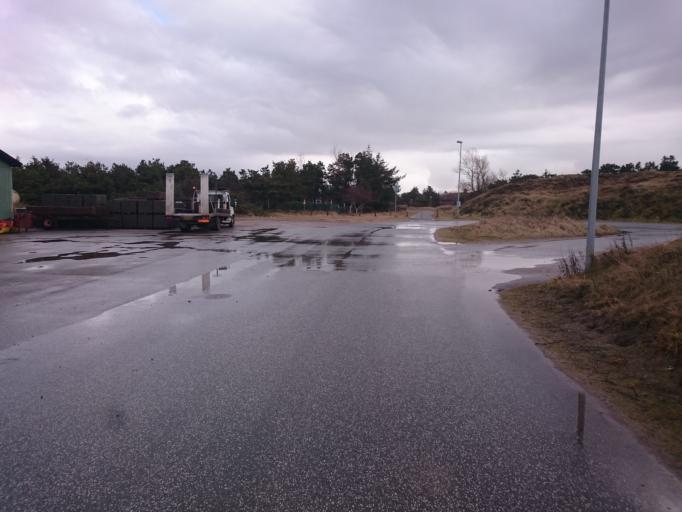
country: DK
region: South Denmark
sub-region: Fano Kommune
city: Nordby
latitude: 55.4416
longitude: 8.3895
